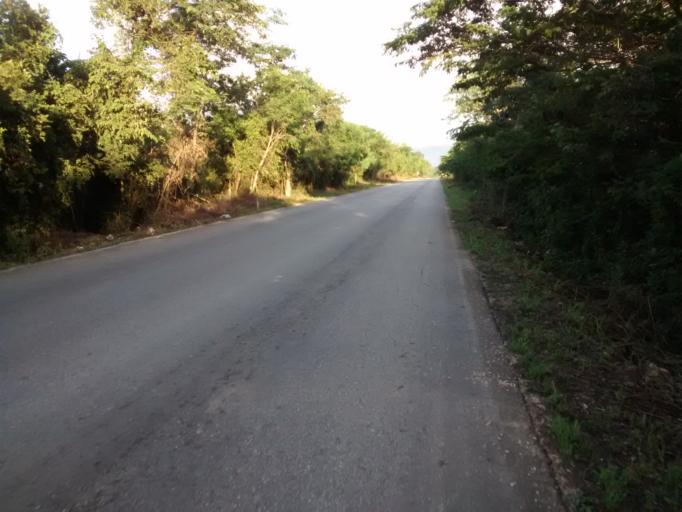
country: MX
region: Yucatan
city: Valladolid
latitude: 20.7311
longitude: -88.2114
